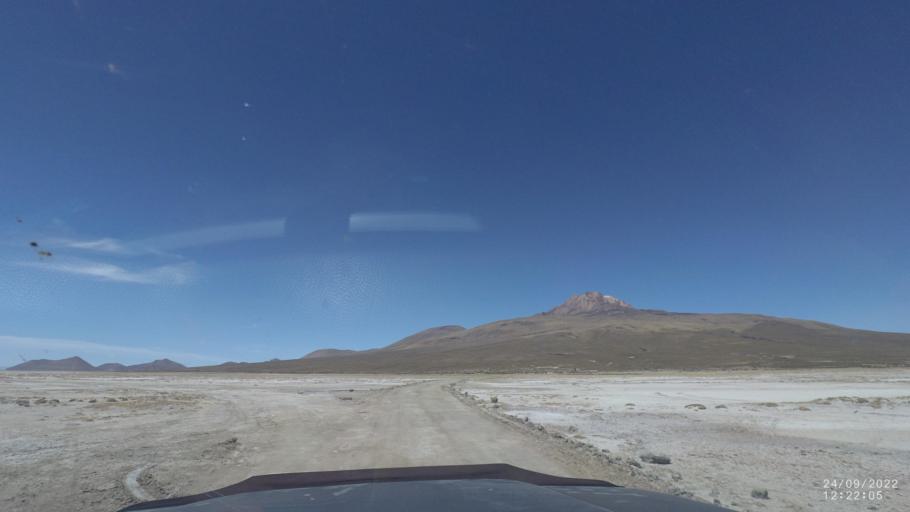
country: BO
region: Potosi
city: Colchani
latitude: -19.7535
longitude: -67.6668
